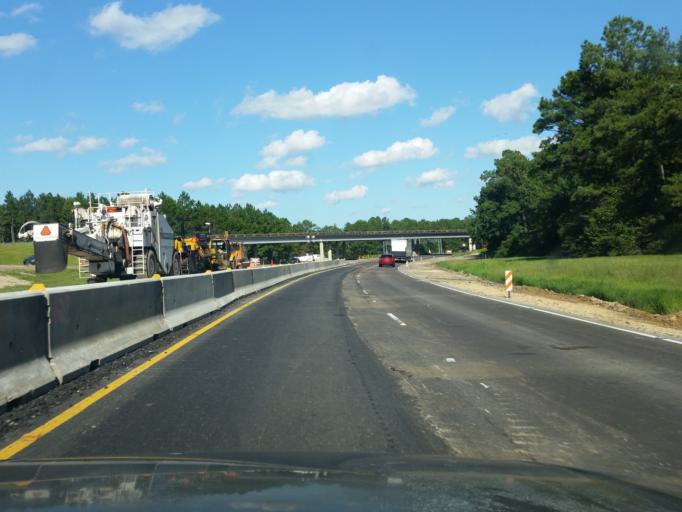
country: US
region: Louisiana
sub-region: Saint Tammany Parish
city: Slidell
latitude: 30.3039
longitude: -89.7391
